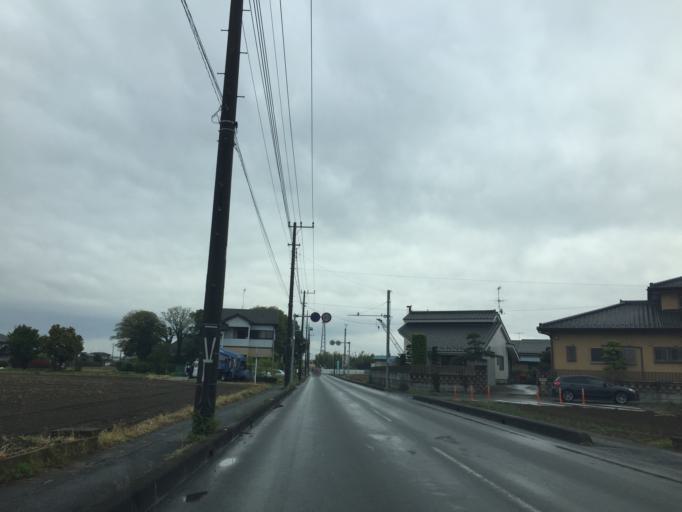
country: JP
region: Saitama
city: Kamifukuoka
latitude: 35.8853
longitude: 139.5580
